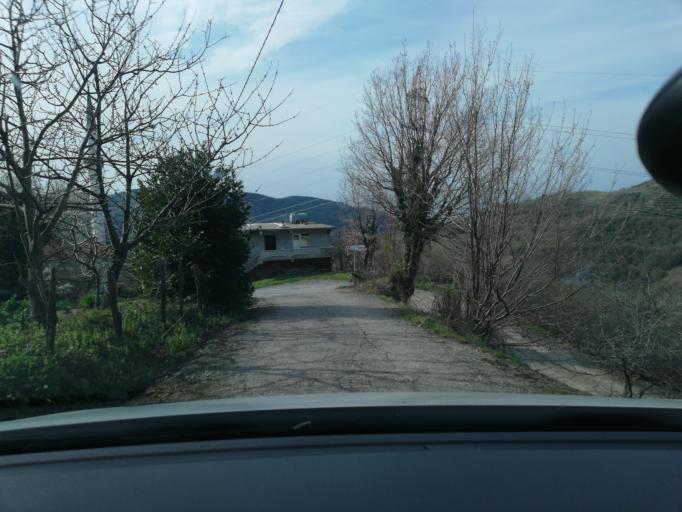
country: TR
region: Zonguldak
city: Kozlu
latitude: 41.3573
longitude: 31.6277
